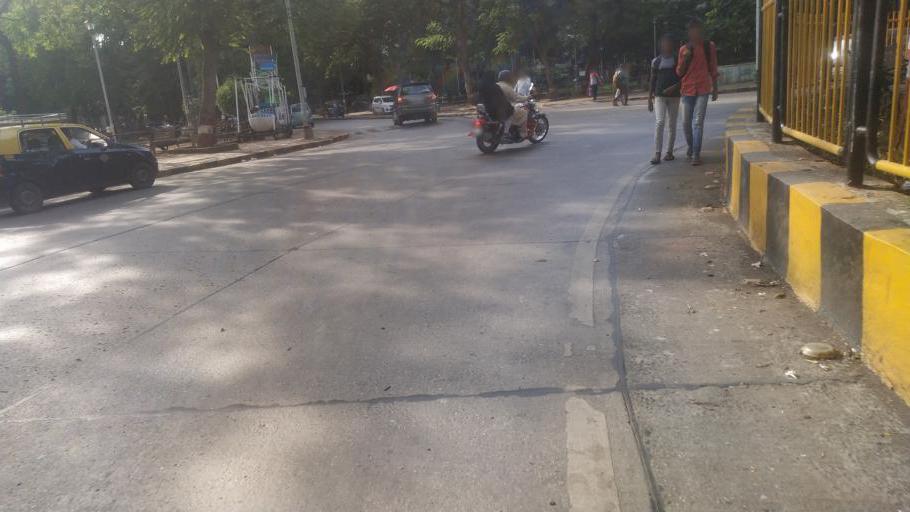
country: IN
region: Maharashtra
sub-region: Mumbai Suburban
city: Mumbai
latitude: 19.0202
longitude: 72.8536
